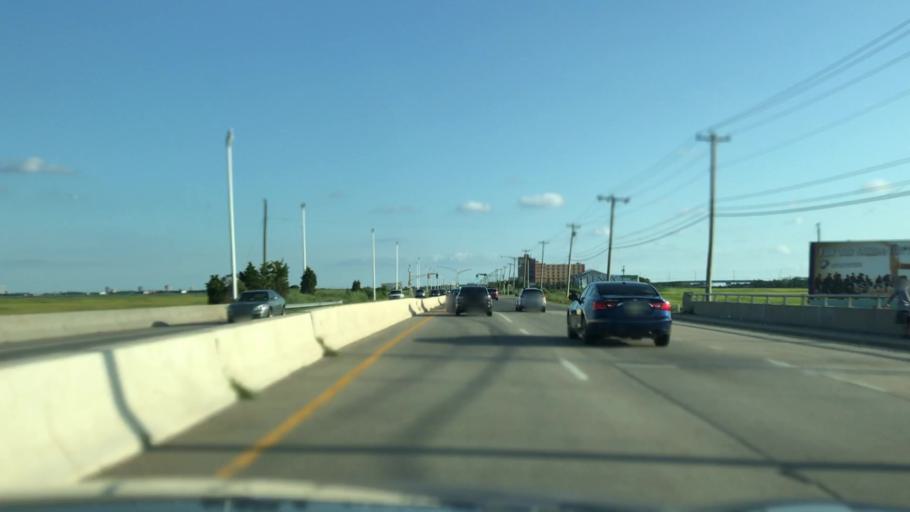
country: US
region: New Jersey
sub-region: Atlantic County
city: Absecon
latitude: 39.4099
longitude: -74.4917
